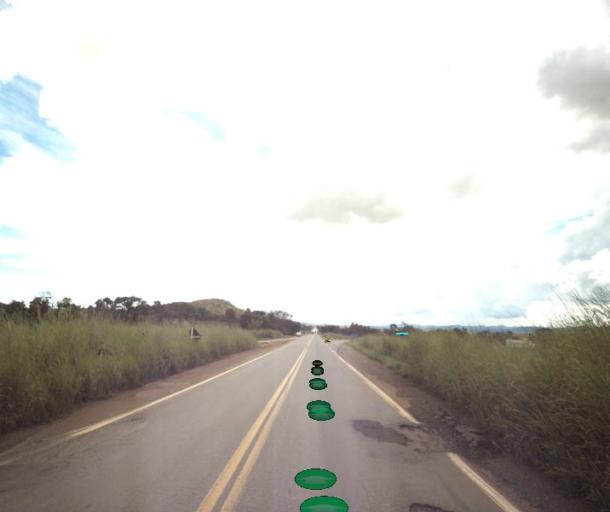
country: BR
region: Goias
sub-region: Jaragua
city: Jaragua
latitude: -15.8926
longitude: -49.2378
